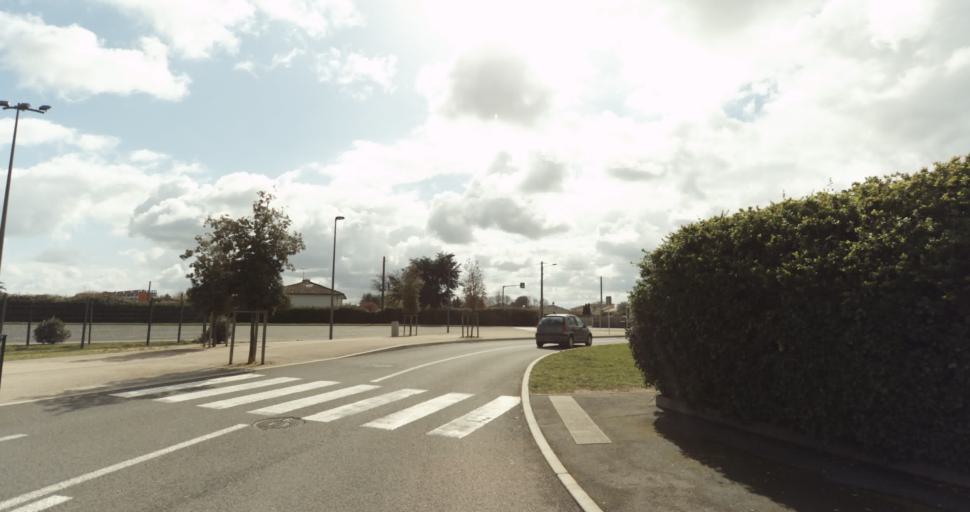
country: FR
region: Midi-Pyrenees
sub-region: Departement de la Haute-Garonne
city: Auterive
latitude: 43.3555
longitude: 1.4646
